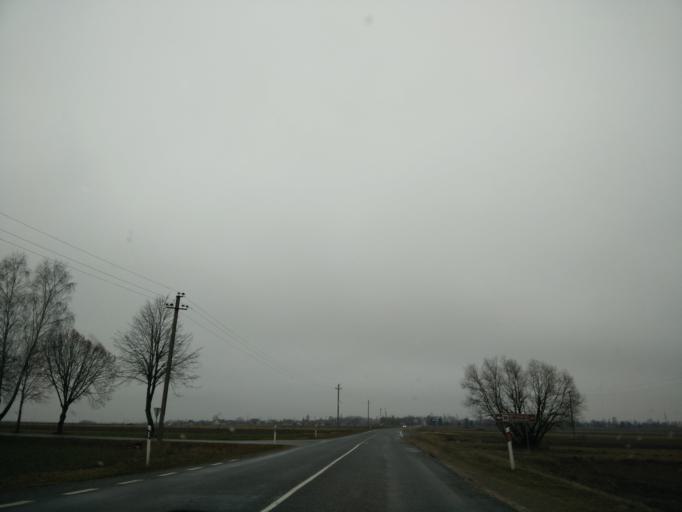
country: LT
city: Ariogala
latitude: 55.3523
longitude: 23.3819
